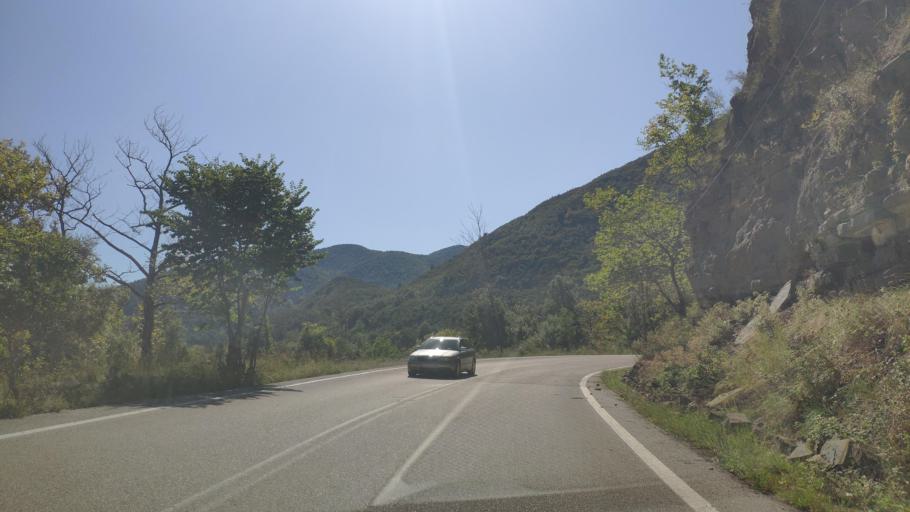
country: GR
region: West Greece
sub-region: Nomos Aitolias kai Akarnanias
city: Sardinia
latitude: 38.9240
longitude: 21.3575
